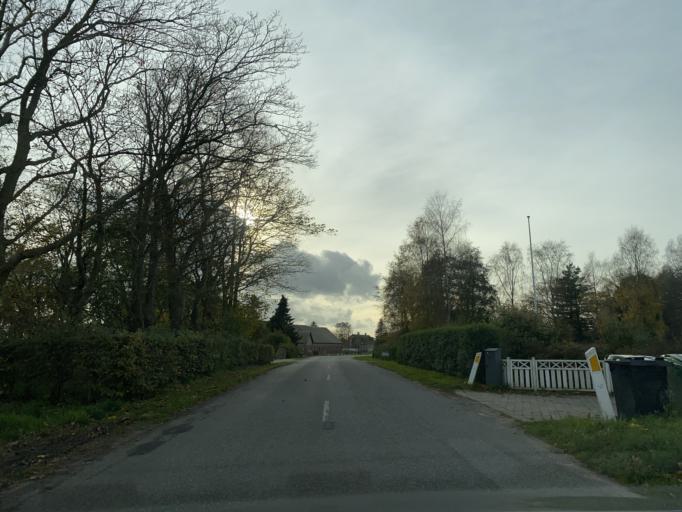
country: DK
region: Central Jutland
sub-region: Skanderborg Kommune
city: Skovby
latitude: 56.1626
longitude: 9.9807
